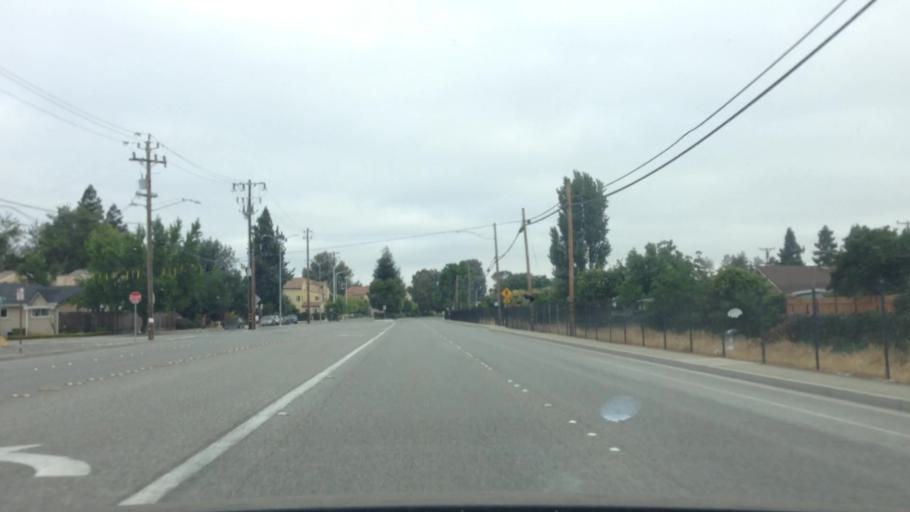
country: US
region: California
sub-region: Alameda County
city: Fremont
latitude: 37.5206
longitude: -121.9560
